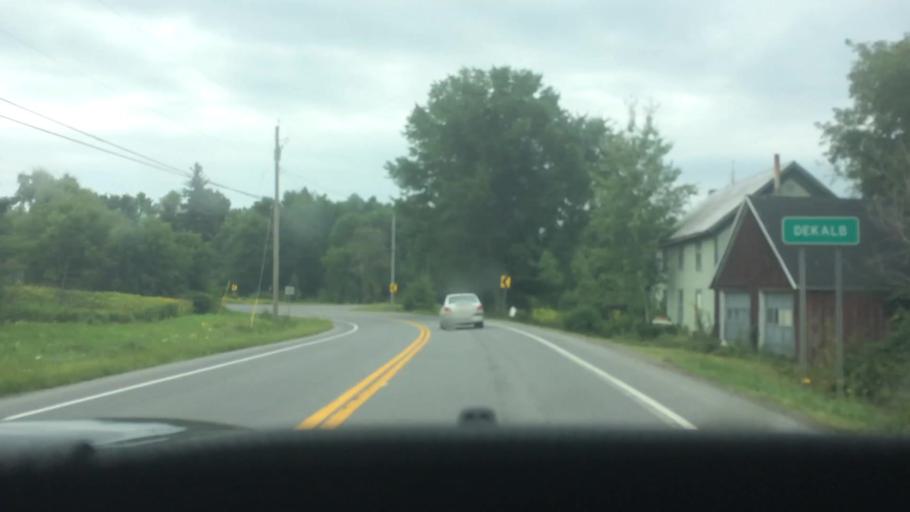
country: US
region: New York
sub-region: St. Lawrence County
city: Canton
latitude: 44.5018
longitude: -75.3429
